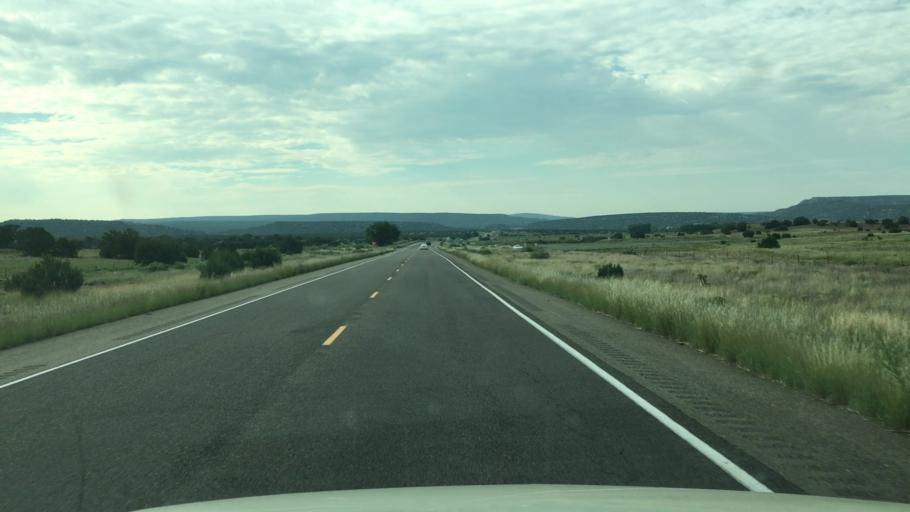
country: US
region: New Mexico
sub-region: Santa Fe County
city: Eldorado at Santa Fe
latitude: 35.4159
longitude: -105.8696
